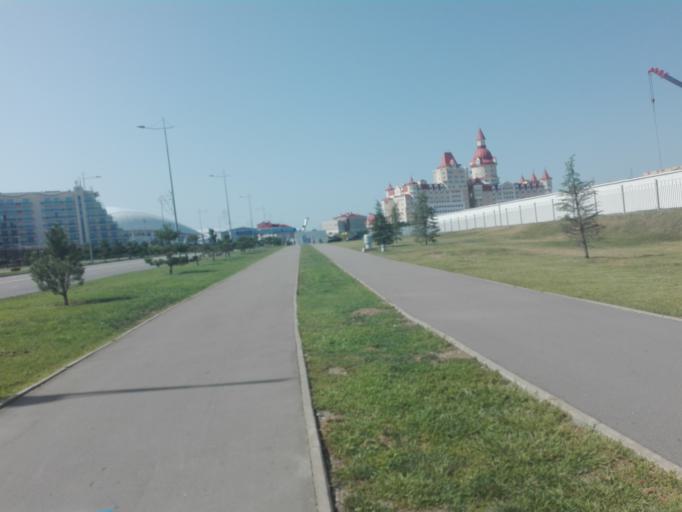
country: RU
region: Krasnodarskiy
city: Adler
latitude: 43.4012
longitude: 39.9674
